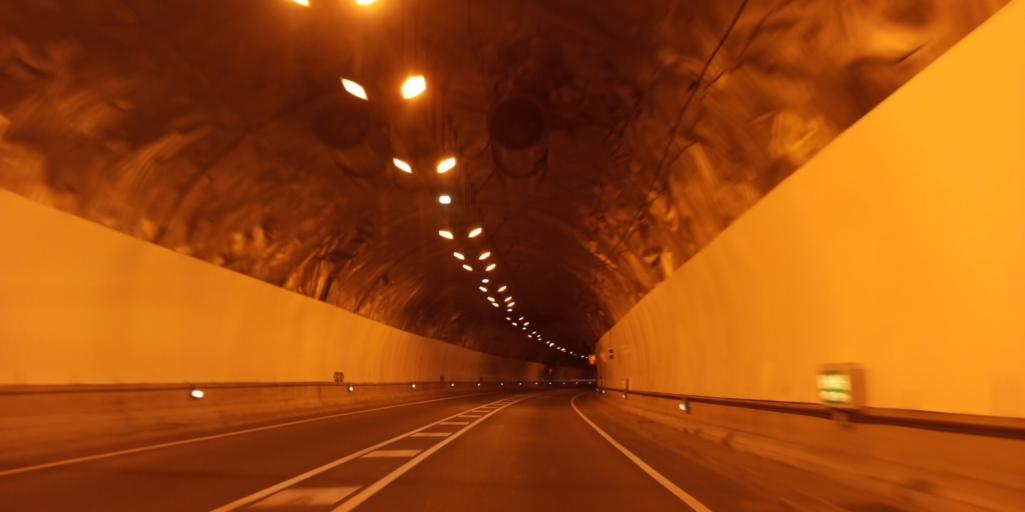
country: ES
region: Catalonia
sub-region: Provincia de Girona
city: Bas
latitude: 42.1247
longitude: 2.4569
